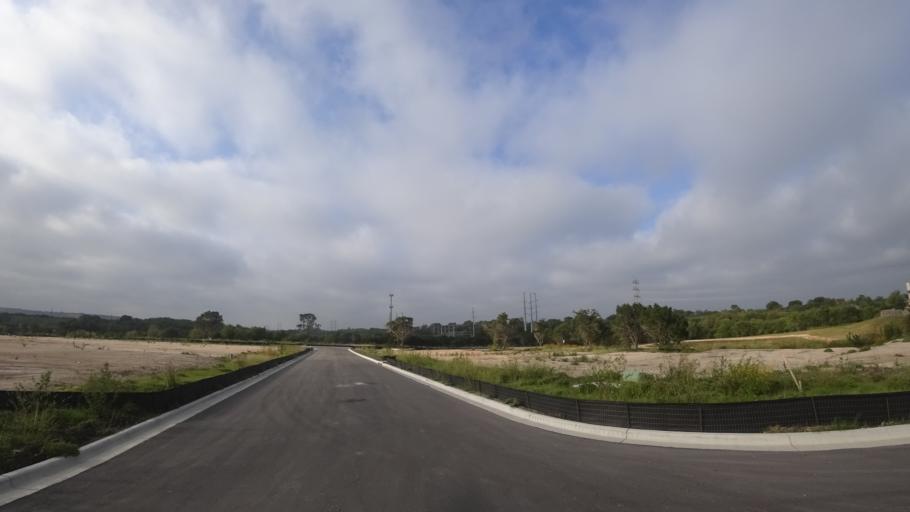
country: US
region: Texas
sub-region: Travis County
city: Pflugerville
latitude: 30.3555
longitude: -97.6437
